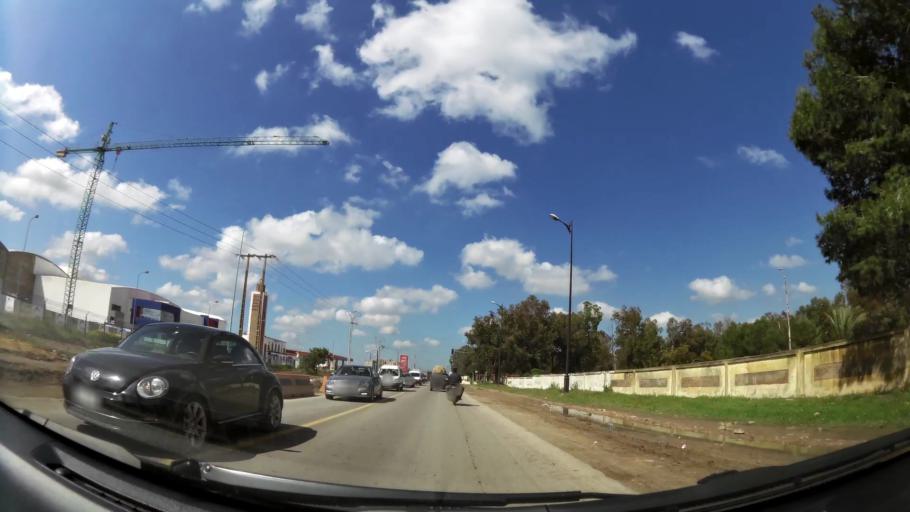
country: MA
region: Grand Casablanca
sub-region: Mediouna
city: Mediouna
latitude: 33.4037
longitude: -7.5340
